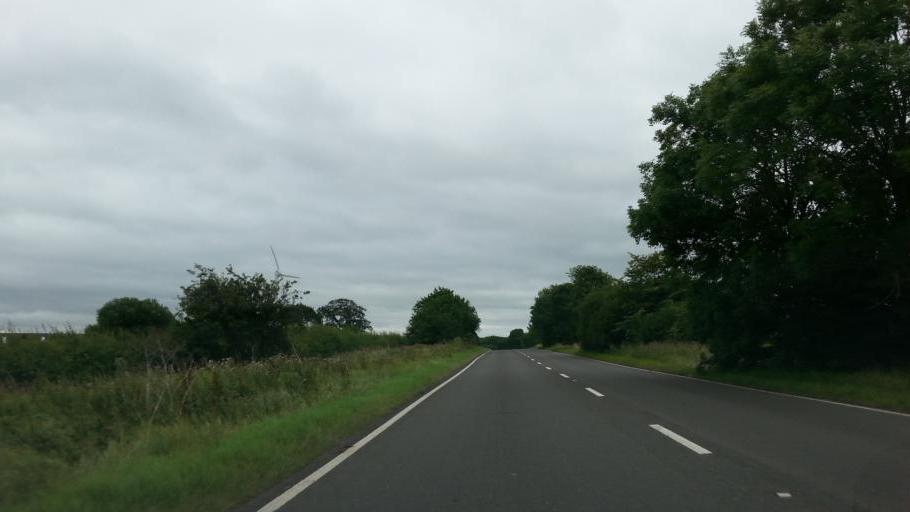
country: GB
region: England
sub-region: Nottinghamshire
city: Farndon
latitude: 53.1224
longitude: -0.8745
